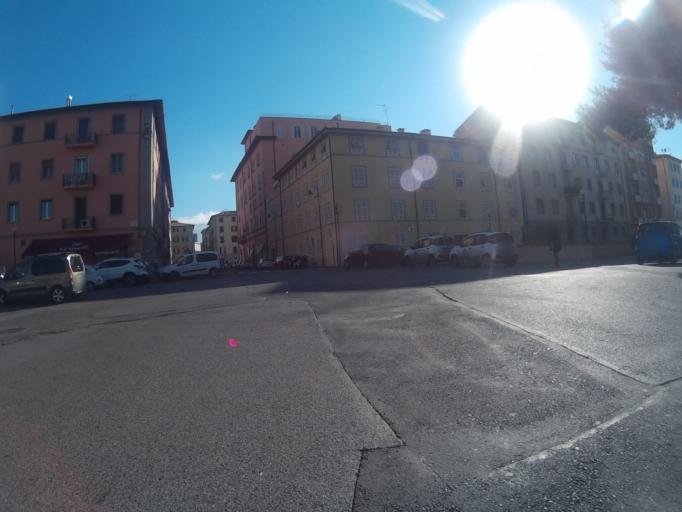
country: IT
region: Tuscany
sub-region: Provincia di Livorno
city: Livorno
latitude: 43.5543
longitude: 10.3053
